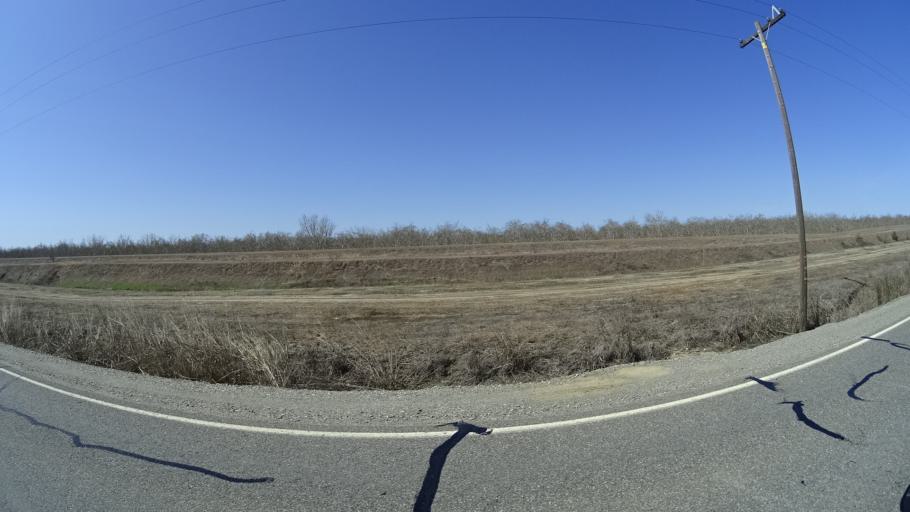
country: US
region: California
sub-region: Glenn County
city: Hamilton City
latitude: 39.7538
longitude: -122.0230
